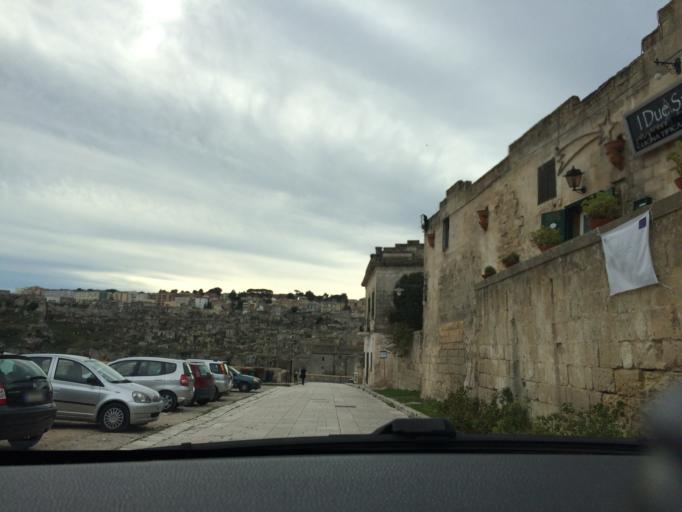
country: IT
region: Basilicate
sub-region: Provincia di Matera
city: Matera
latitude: 40.6665
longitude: 16.6136
